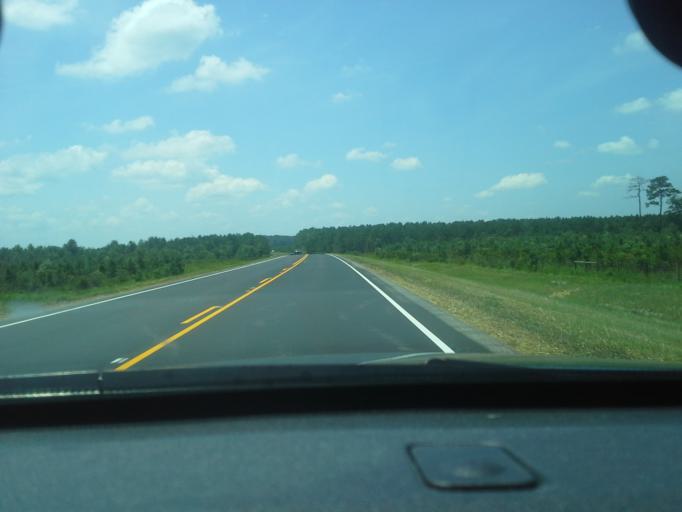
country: US
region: North Carolina
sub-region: Chowan County
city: Edenton
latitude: 35.9239
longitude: -76.5207
